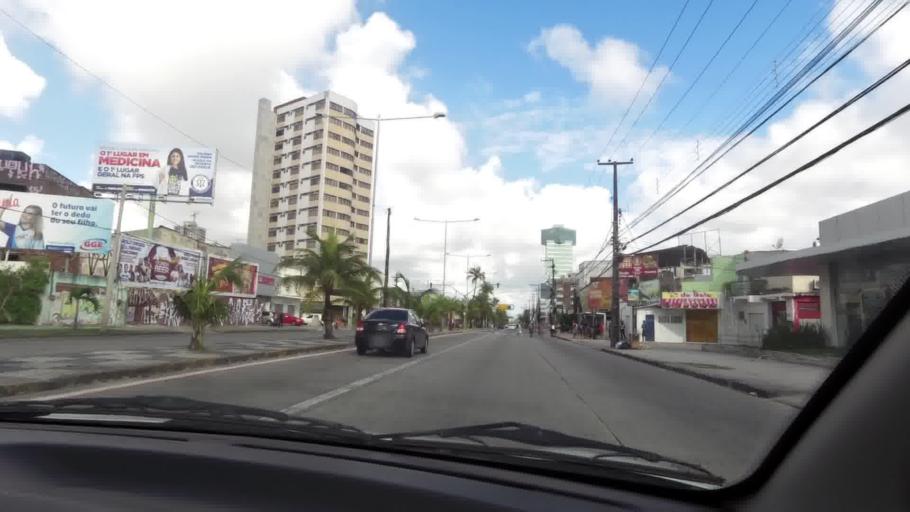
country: BR
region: Pernambuco
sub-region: Recife
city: Recife
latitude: -8.0881
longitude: -34.8840
